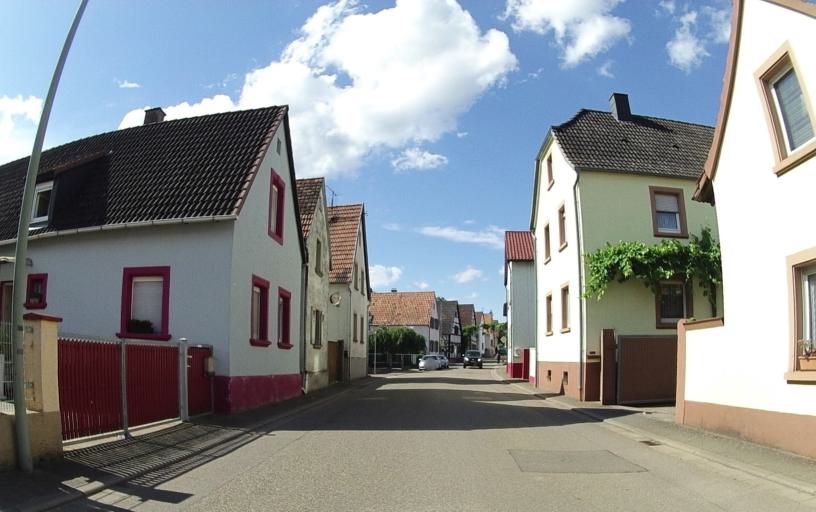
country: DE
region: Rheinland-Pfalz
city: Steinfeld
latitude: 49.0472
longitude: 8.0366
